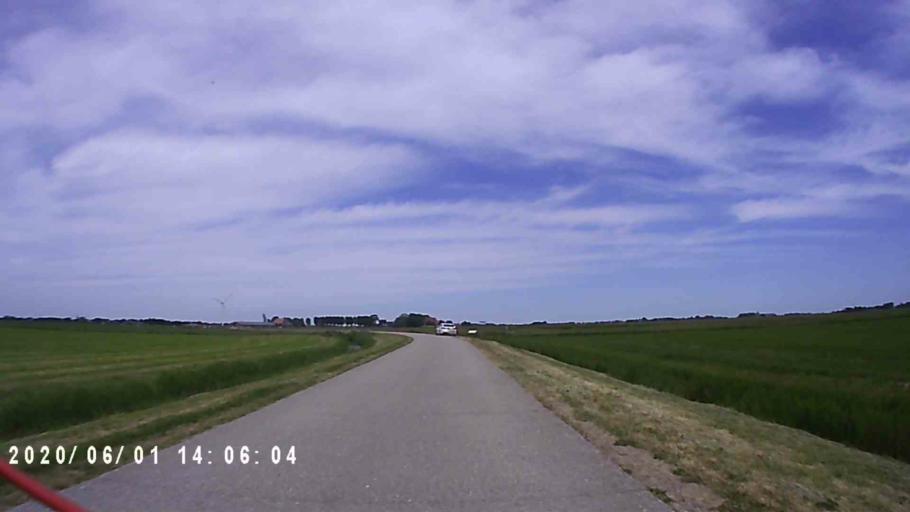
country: NL
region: Friesland
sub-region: Gemeente Littenseradiel
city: Winsum
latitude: 53.1166
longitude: 5.6380
